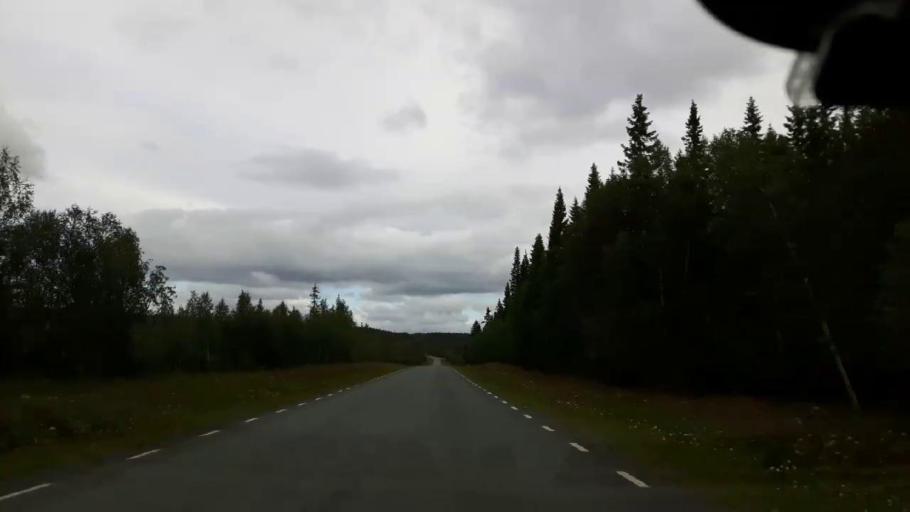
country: SE
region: Jaemtland
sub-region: Krokoms Kommun
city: Valla
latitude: 63.5624
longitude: 13.8465
